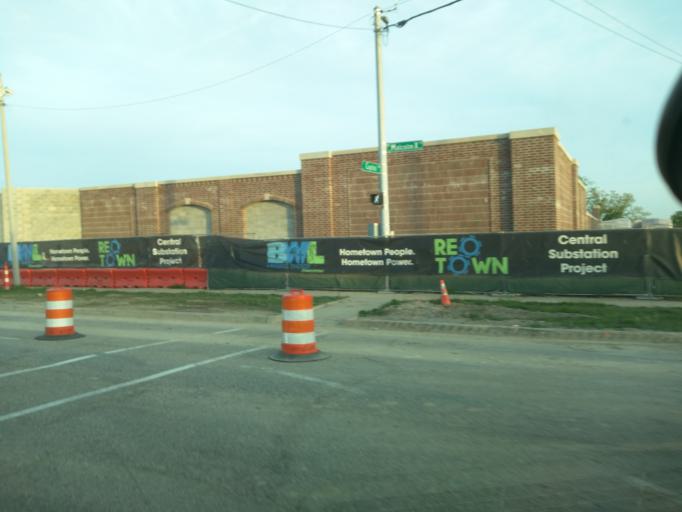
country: US
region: Michigan
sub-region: Ingham County
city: Lansing
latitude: 42.7256
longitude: -84.5539
